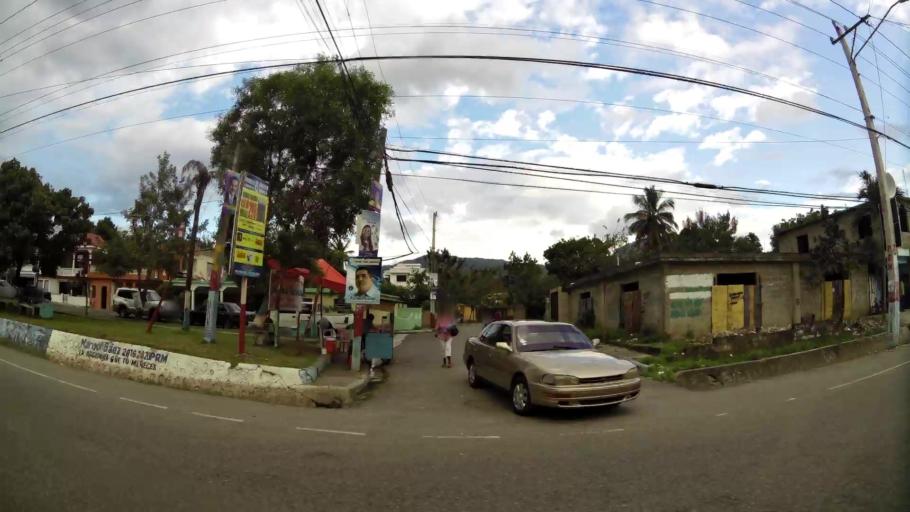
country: DO
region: San Cristobal
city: Villa Altagracia
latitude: 18.6814
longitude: -70.1785
